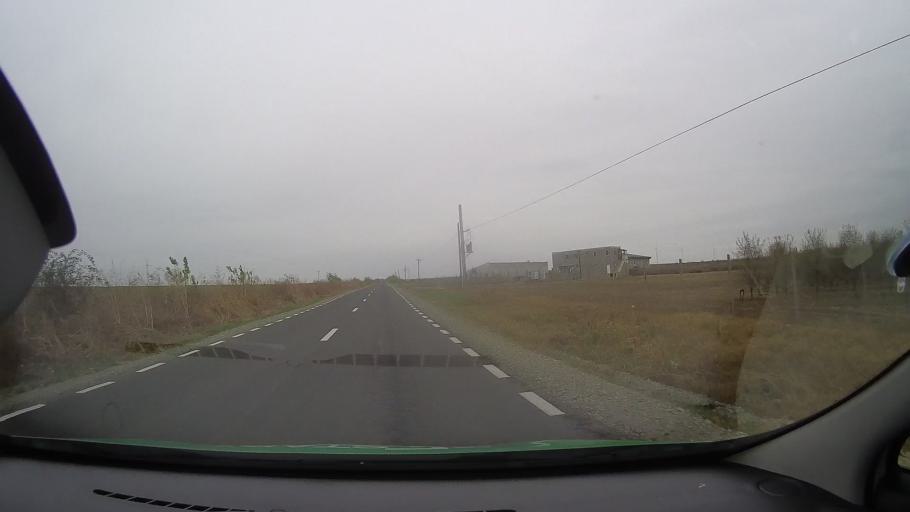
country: RO
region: Constanta
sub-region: Comuna Tortoman
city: Tortoman
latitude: 44.3665
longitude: 28.2082
